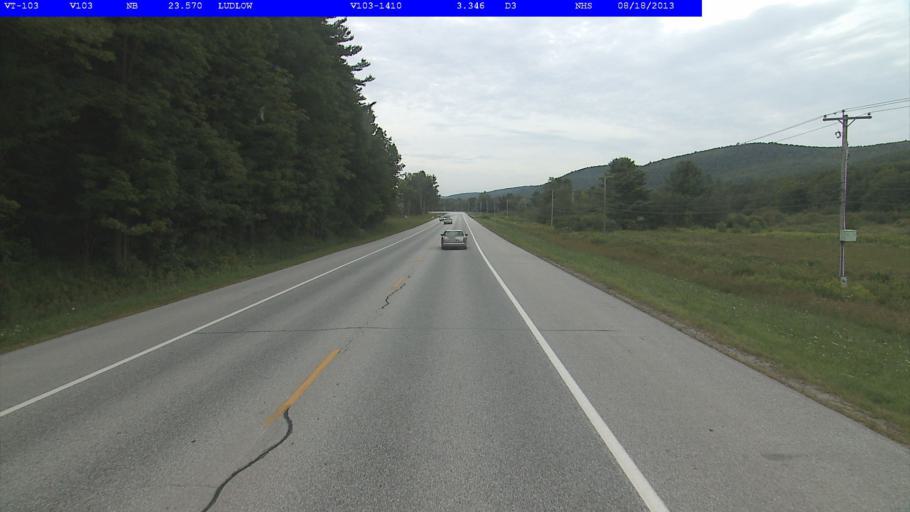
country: US
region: Vermont
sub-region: Windsor County
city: Chester
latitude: 43.4103
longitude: -72.7067
